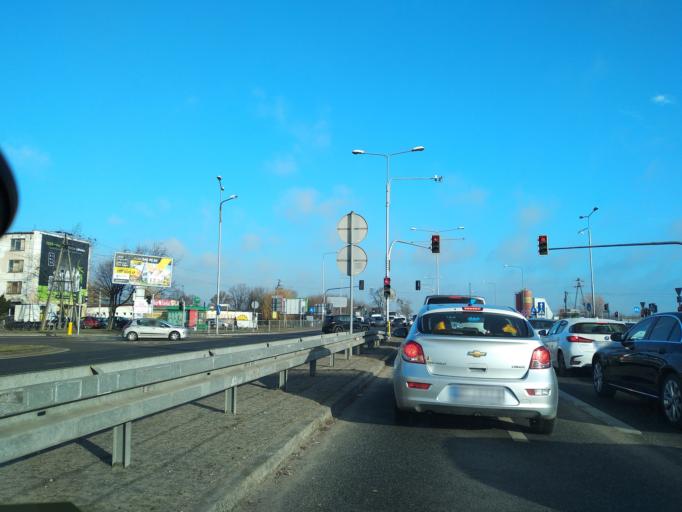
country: PL
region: Masovian Voivodeship
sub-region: Powiat piaseczynski
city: Mysiadlo
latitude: 52.0974
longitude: 21.0190
